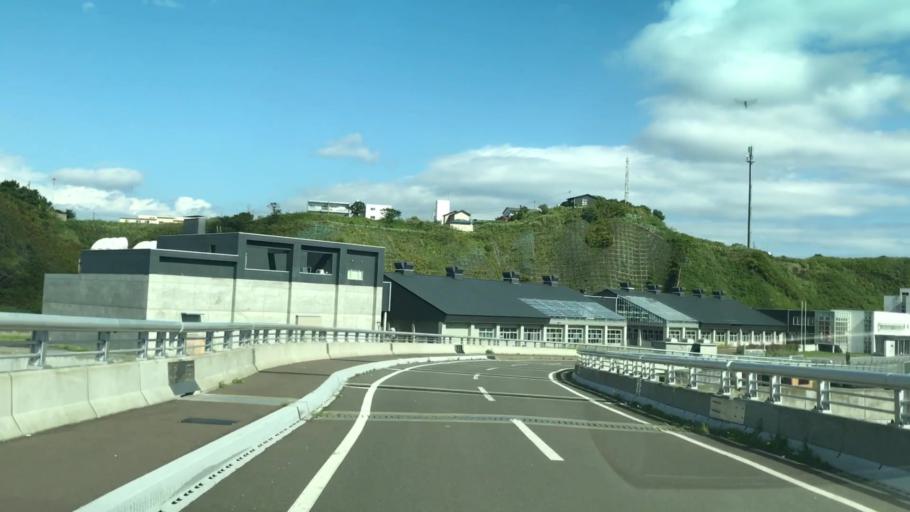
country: JP
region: Hokkaido
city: Muroran
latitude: 42.3098
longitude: 140.9651
